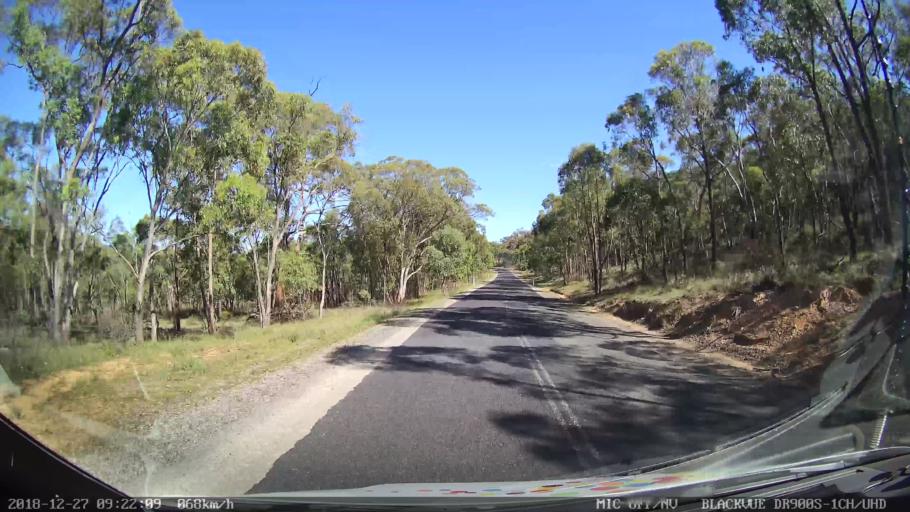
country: AU
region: New South Wales
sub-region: Lithgow
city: Portland
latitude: -33.1273
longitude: 150.0110
